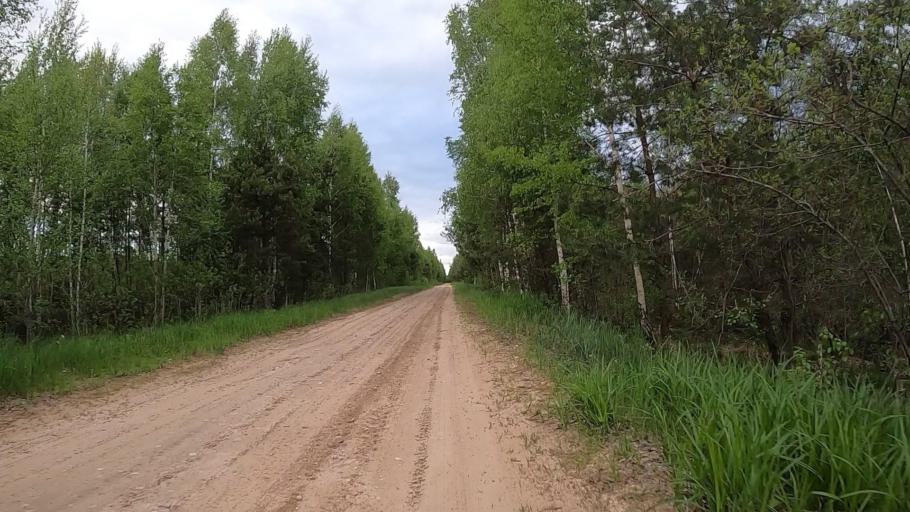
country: LV
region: Olaine
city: Olaine
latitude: 56.8400
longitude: 23.9291
